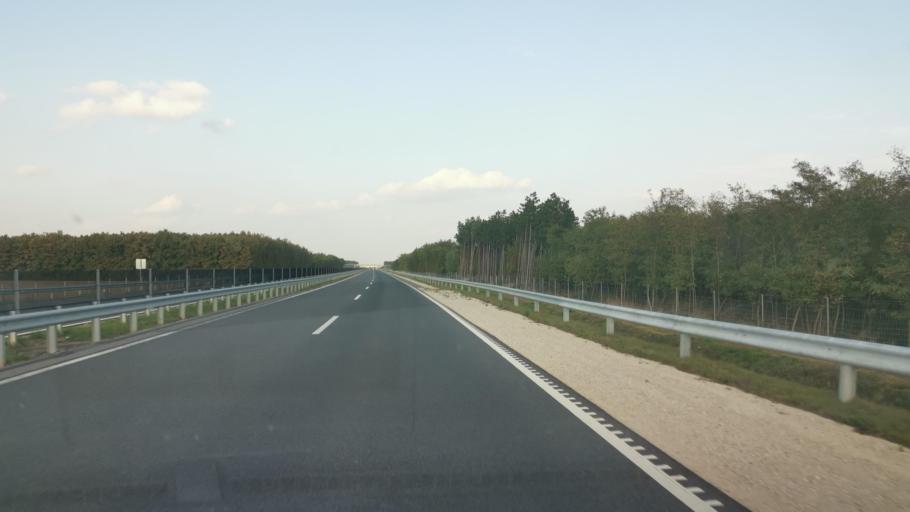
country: HU
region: Gyor-Moson-Sopron
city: Fertoszentmiklos
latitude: 47.5594
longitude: 16.8902
